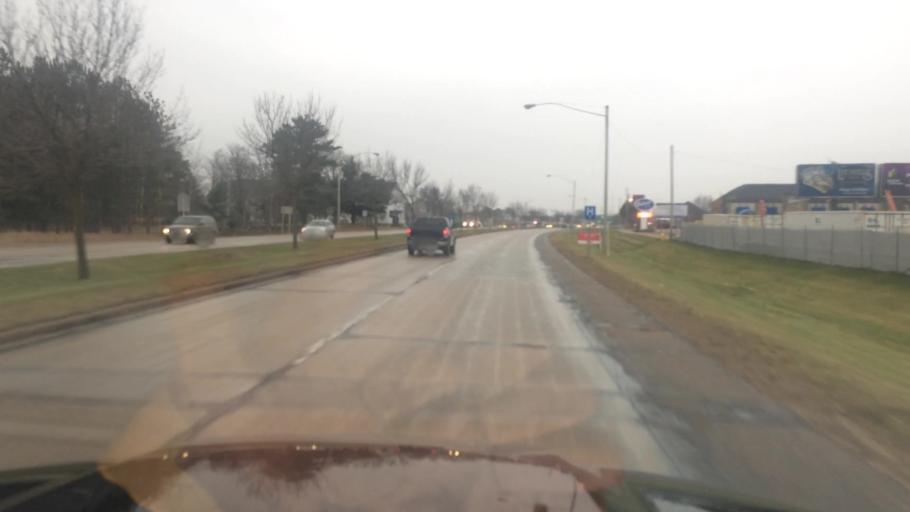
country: US
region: Wisconsin
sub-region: Portage County
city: Stevens Point
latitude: 44.5404
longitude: -89.5757
